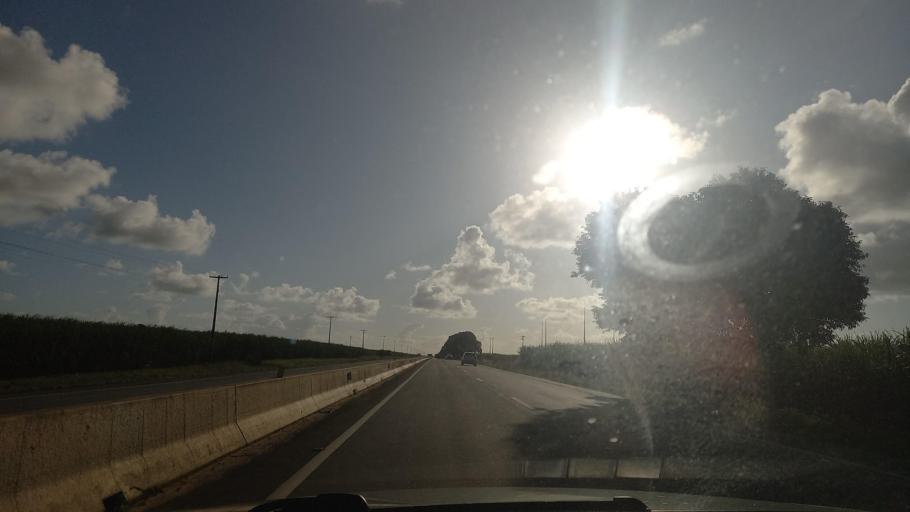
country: BR
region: Alagoas
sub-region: Sao Miguel Dos Campos
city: Sao Miguel dos Campos
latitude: -9.8057
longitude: -36.1247
